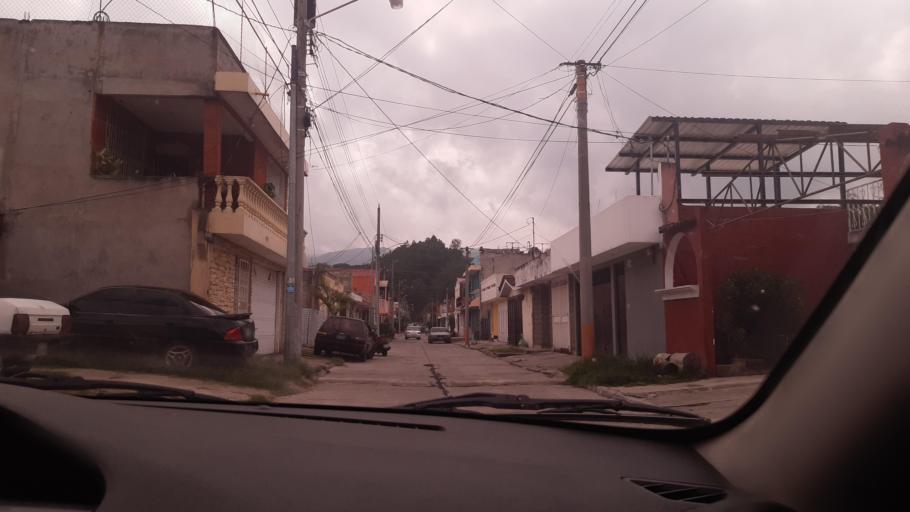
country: GT
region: Guatemala
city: Petapa
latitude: 14.5052
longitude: -90.5463
